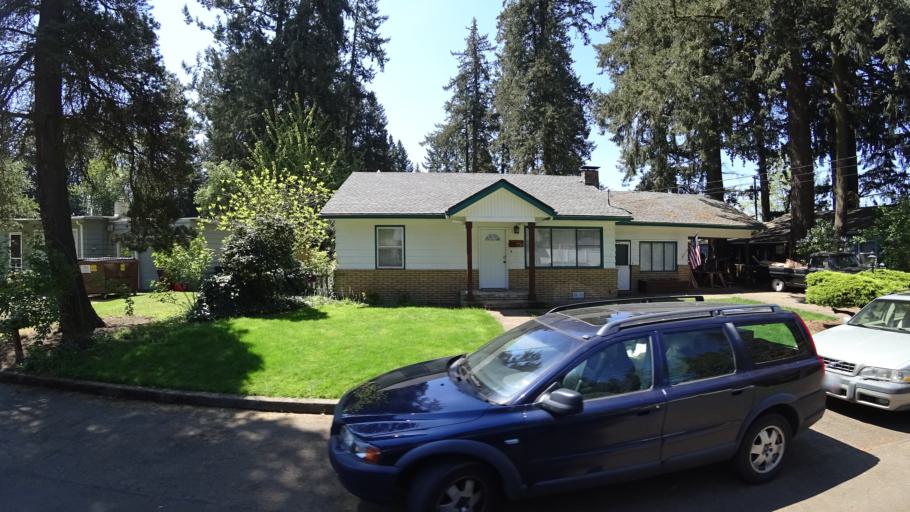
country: US
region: Oregon
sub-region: Washington County
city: Hillsboro
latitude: 45.5126
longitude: -122.9786
